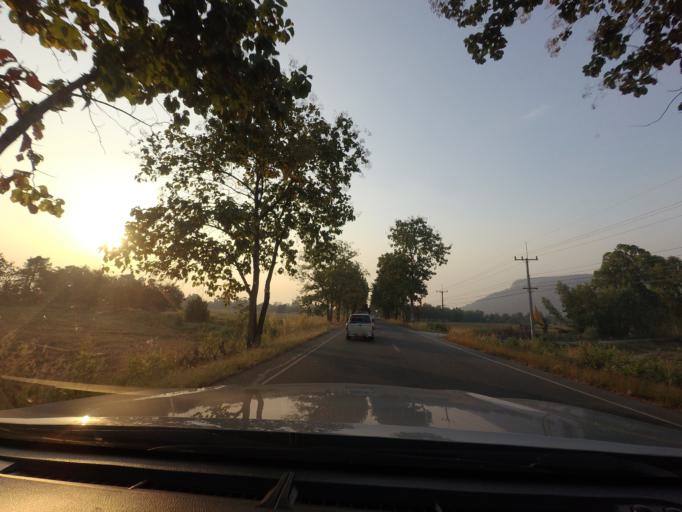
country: TH
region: Phitsanulok
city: Wang Thong
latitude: 16.7082
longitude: 100.4884
